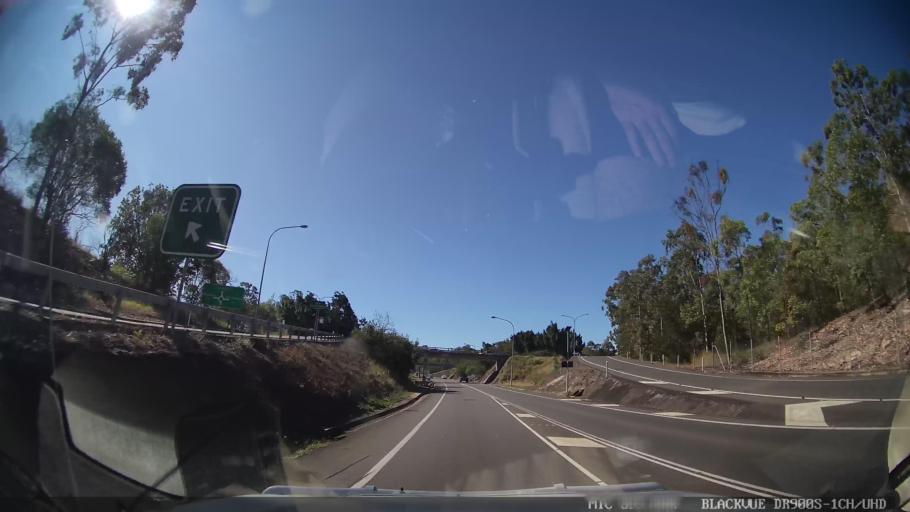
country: AU
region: Queensland
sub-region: Fraser Coast
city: Maryborough
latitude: -25.5208
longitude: 152.6679
